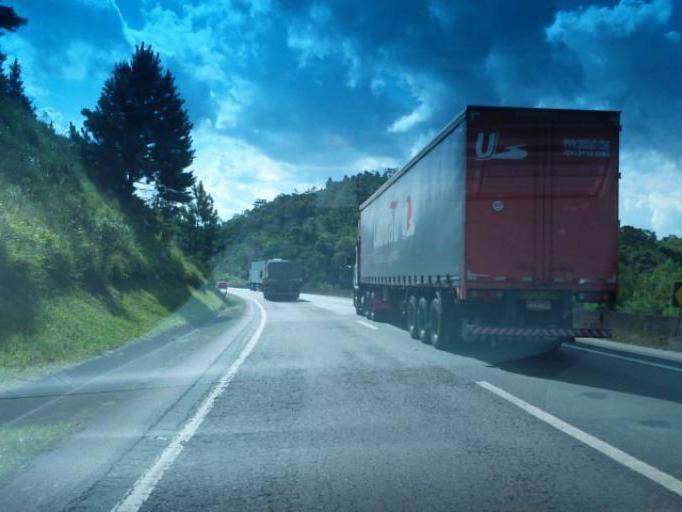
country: BR
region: Parana
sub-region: Campina Grande Do Sul
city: Campina Grande do Sul
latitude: -25.0997
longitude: -48.8134
